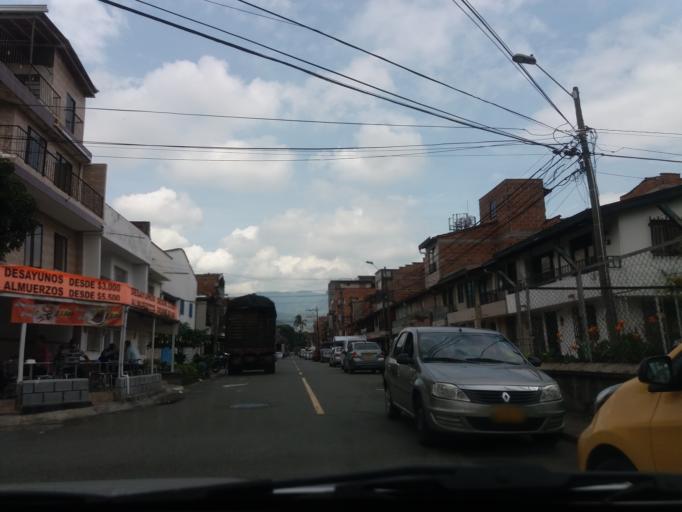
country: CO
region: Antioquia
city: Itagui
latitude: 6.2060
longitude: -75.5825
